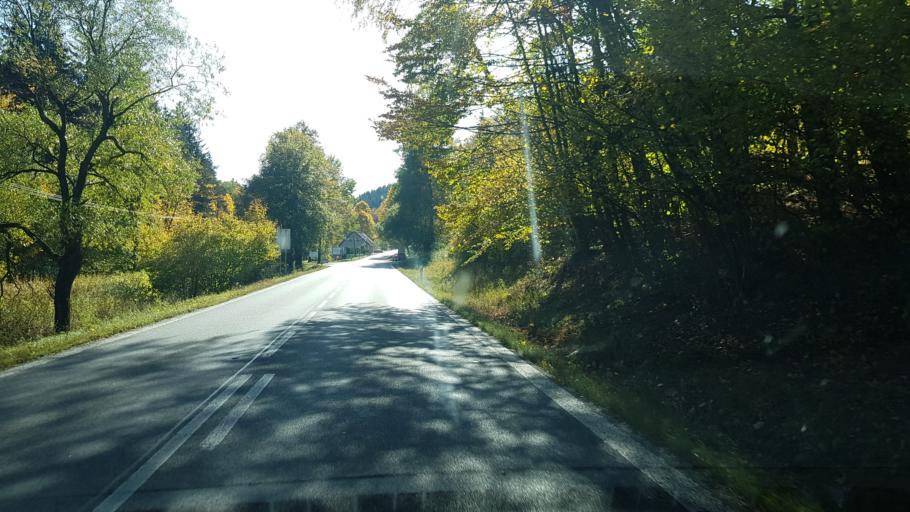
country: CZ
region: Jihocesky
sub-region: Okres Prachatice
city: Vimperk
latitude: 49.0777
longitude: 13.7817
